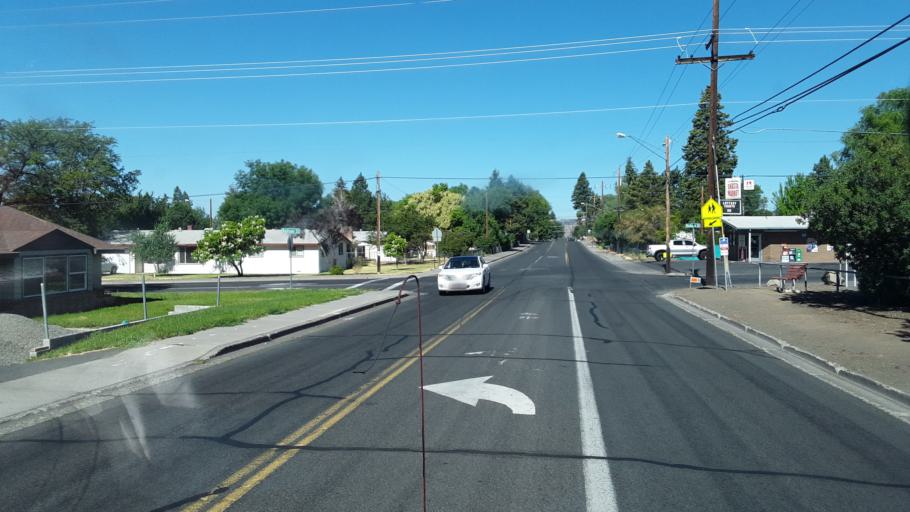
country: US
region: Oregon
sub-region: Klamath County
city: Altamont
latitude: 42.2139
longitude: -121.7172
